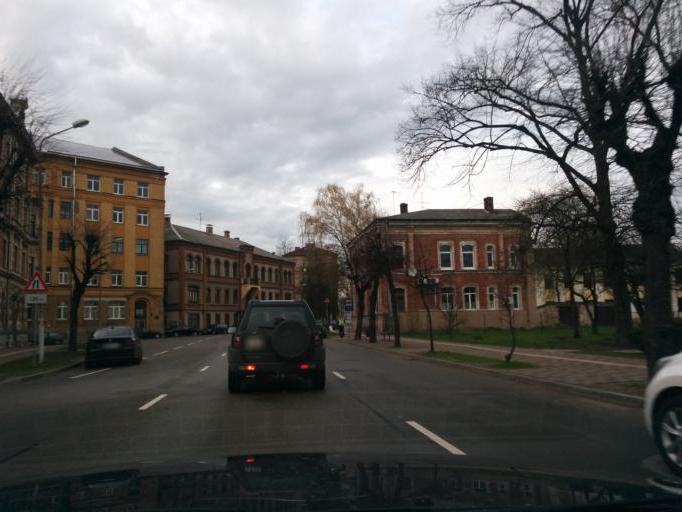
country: LV
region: Jelgava
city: Jelgava
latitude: 56.6456
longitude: 23.7306
